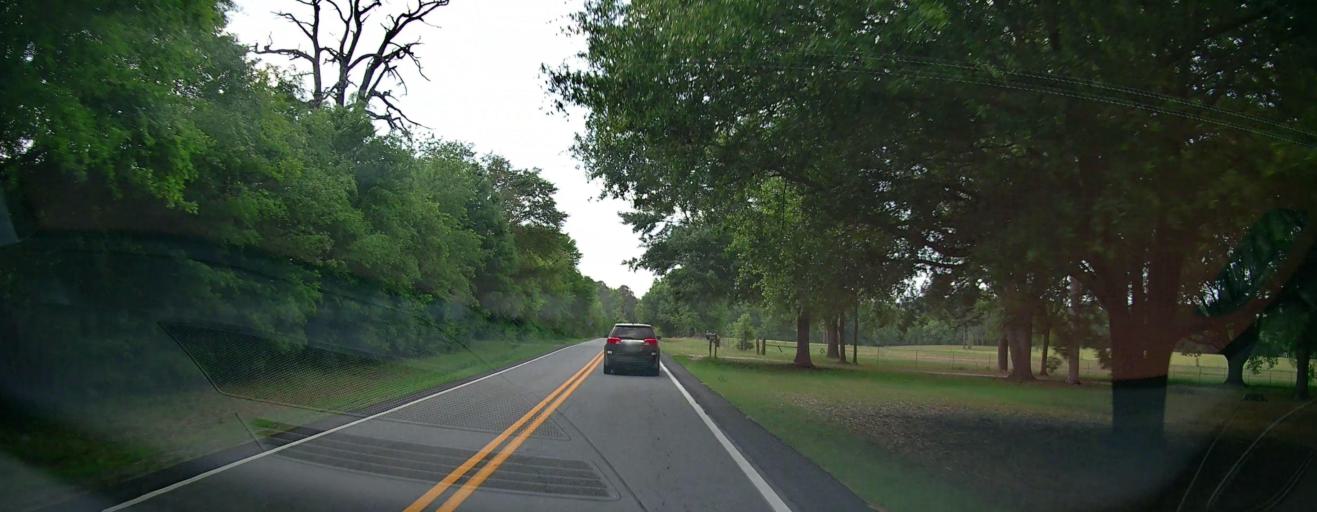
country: US
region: Georgia
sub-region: Laurens County
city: East Dublin
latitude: 32.6302
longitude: -82.8897
